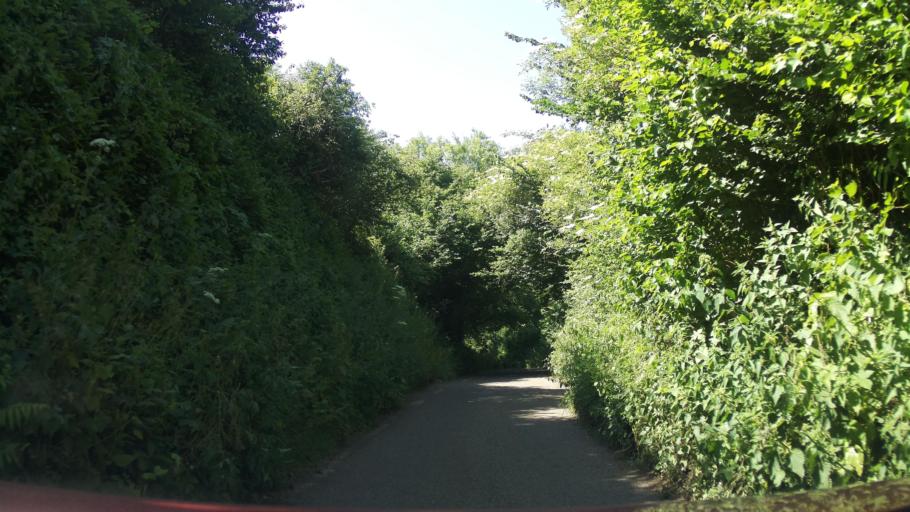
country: GB
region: England
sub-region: Borough of Torbay
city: Paignton
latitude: 50.4153
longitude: -3.5978
